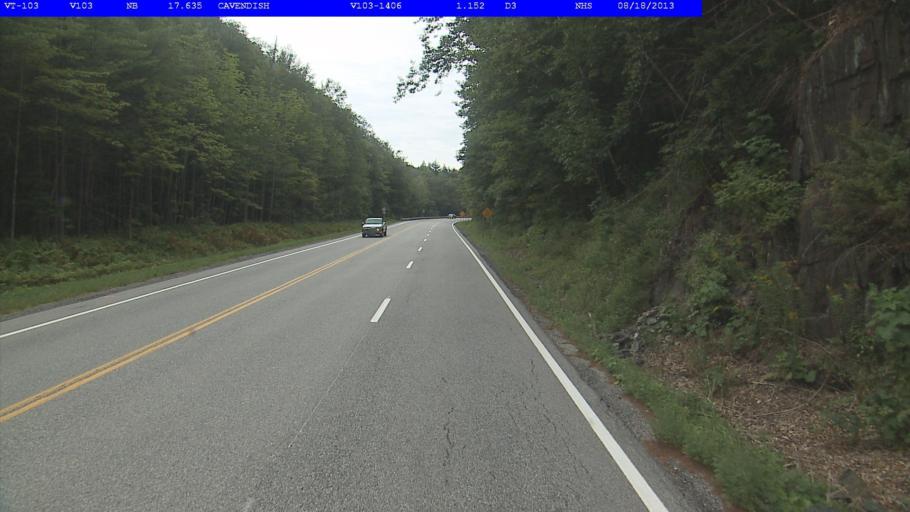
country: US
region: Vermont
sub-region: Windsor County
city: Chester
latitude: 43.3636
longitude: -72.6347
